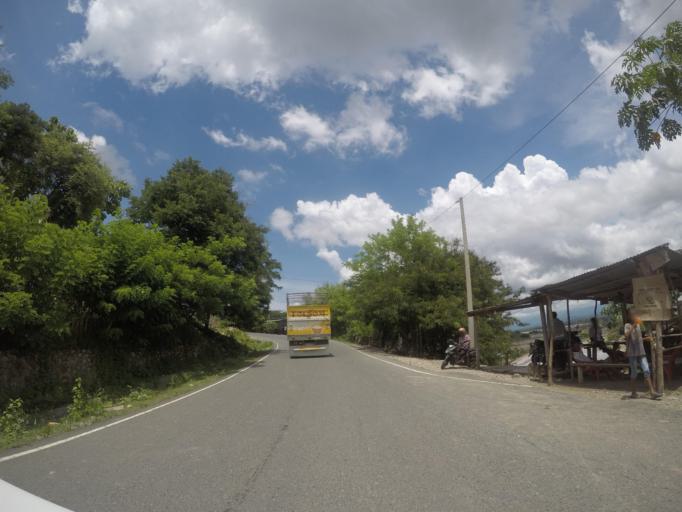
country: TL
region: Bobonaro
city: Maliana
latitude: -8.9528
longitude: 125.1101
